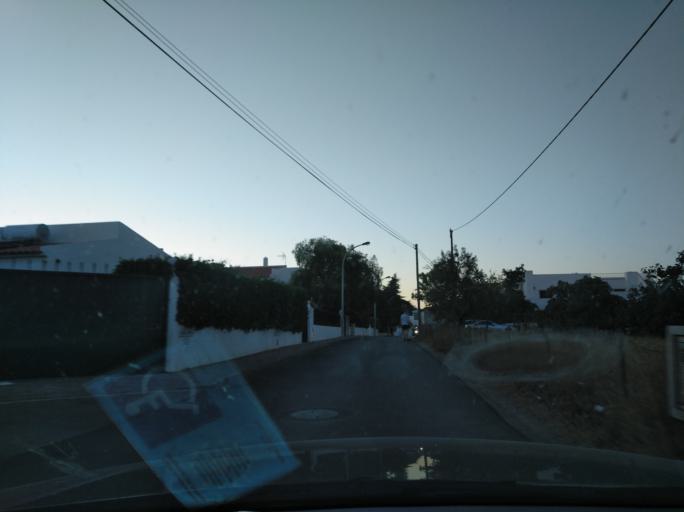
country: PT
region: Faro
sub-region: Tavira
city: Tavira
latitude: 37.1383
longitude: -7.5969
